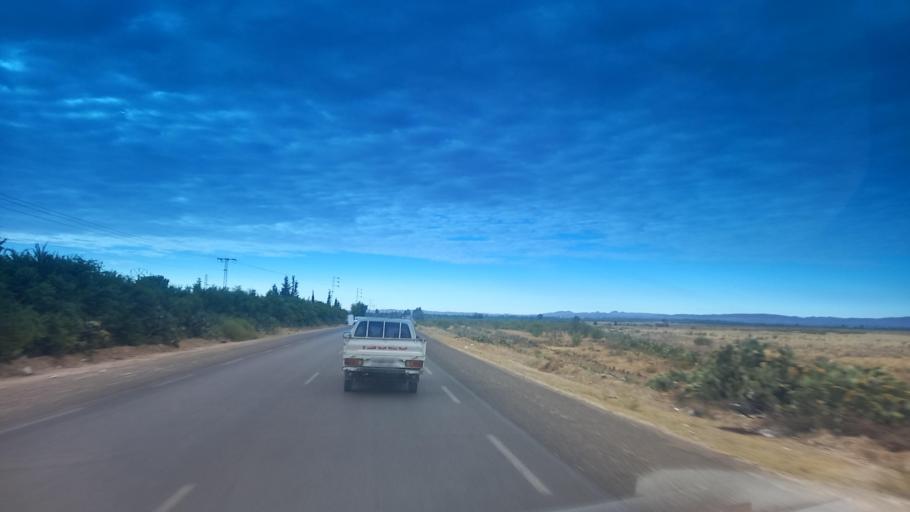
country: TN
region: Al Qasrayn
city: Sbiba
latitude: 35.3142
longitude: 9.0842
